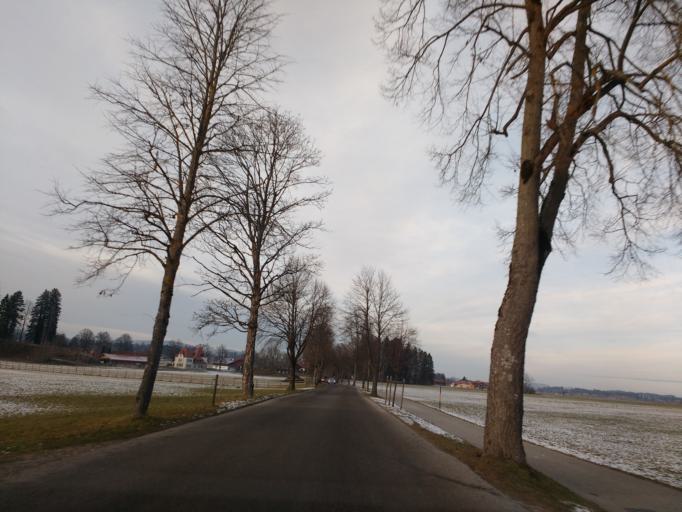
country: DE
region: Bavaria
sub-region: Swabia
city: Schwangau
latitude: 47.5649
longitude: 10.7382
